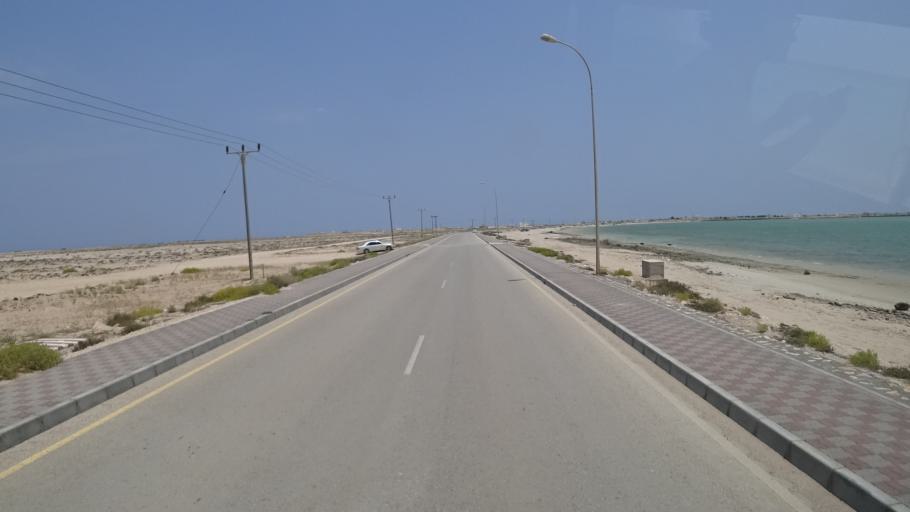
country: OM
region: Ash Sharqiyah
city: Sur
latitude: 22.5291
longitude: 59.7724
